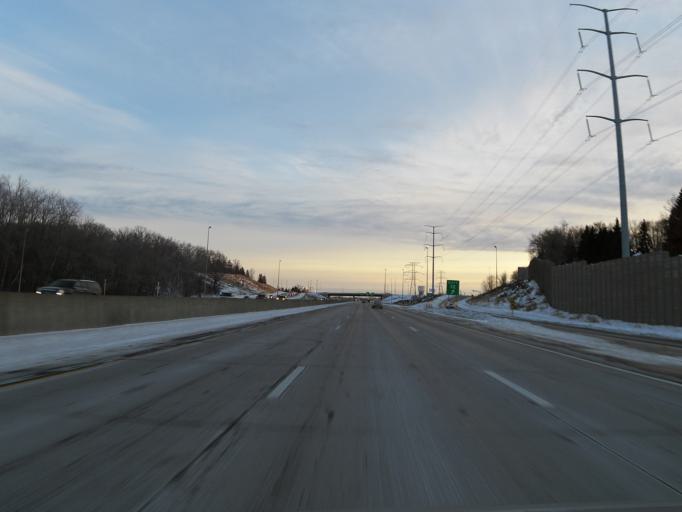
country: US
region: Minnesota
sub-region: Hennepin County
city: Eden Prairie
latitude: 44.8728
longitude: -93.4347
